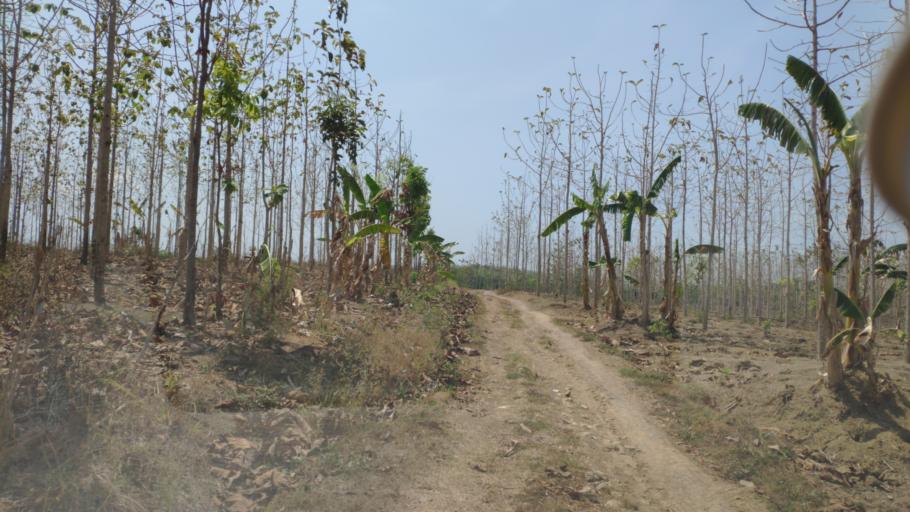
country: ID
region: Central Java
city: Watulumbung
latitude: -7.0207
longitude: 111.5051
